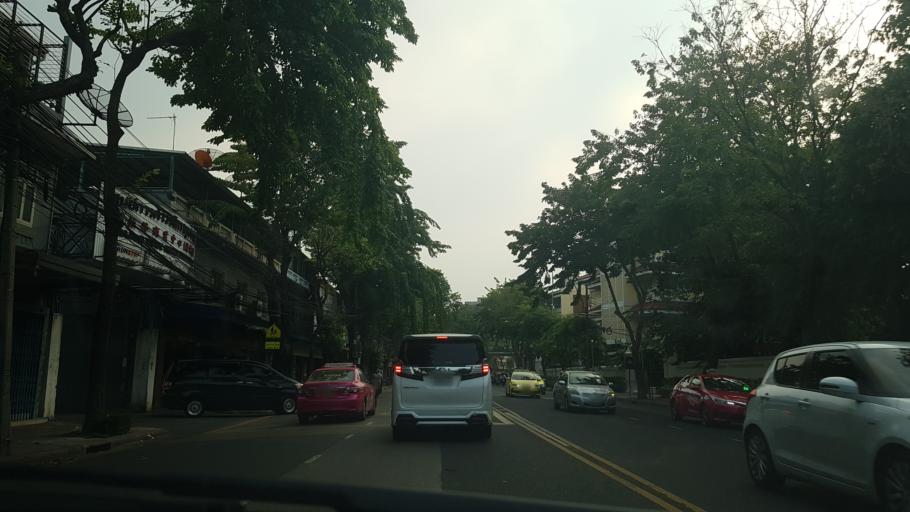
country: TH
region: Bangkok
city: Pom Prap Sattru Phai
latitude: 13.7540
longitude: 100.5094
